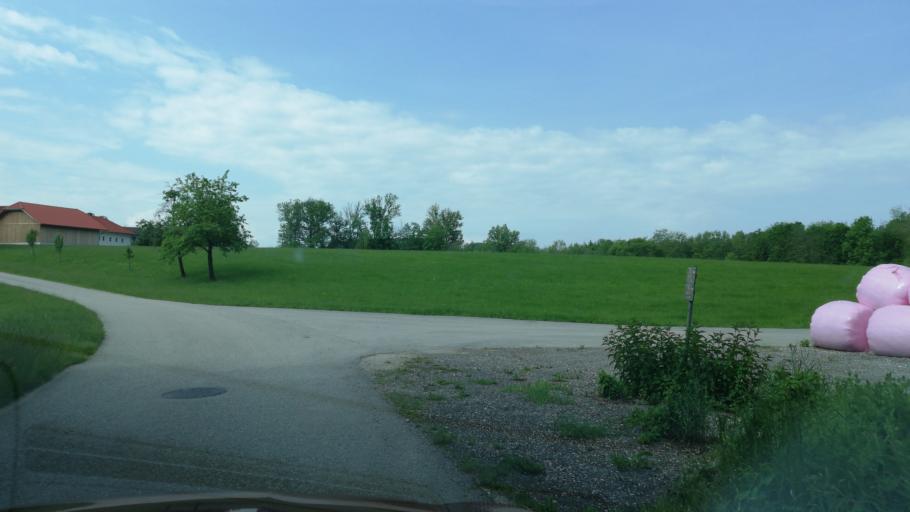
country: AT
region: Upper Austria
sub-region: Politischer Bezirk Steyr-Land
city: Bad Hall
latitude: 48.0487
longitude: 14.2091
